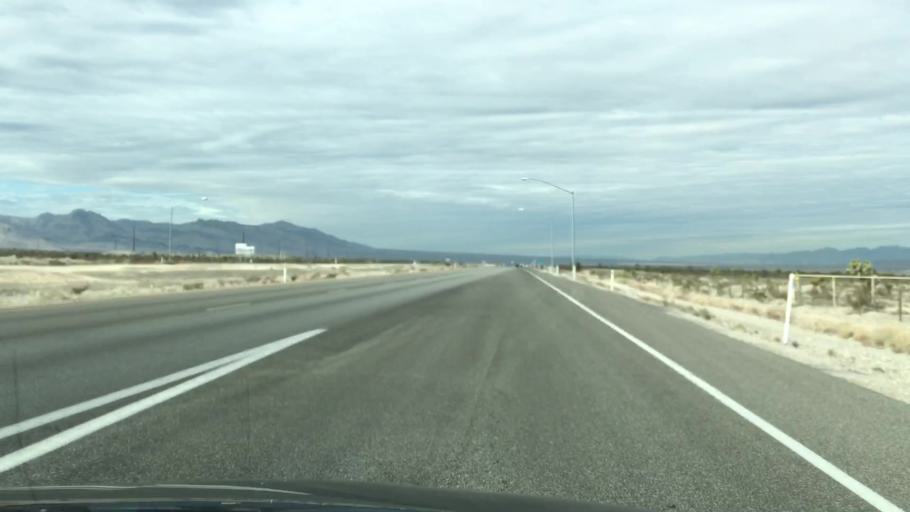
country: US
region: Nevada
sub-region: Clark County
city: Summerlin South
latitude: 36.3648
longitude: -115.3538
